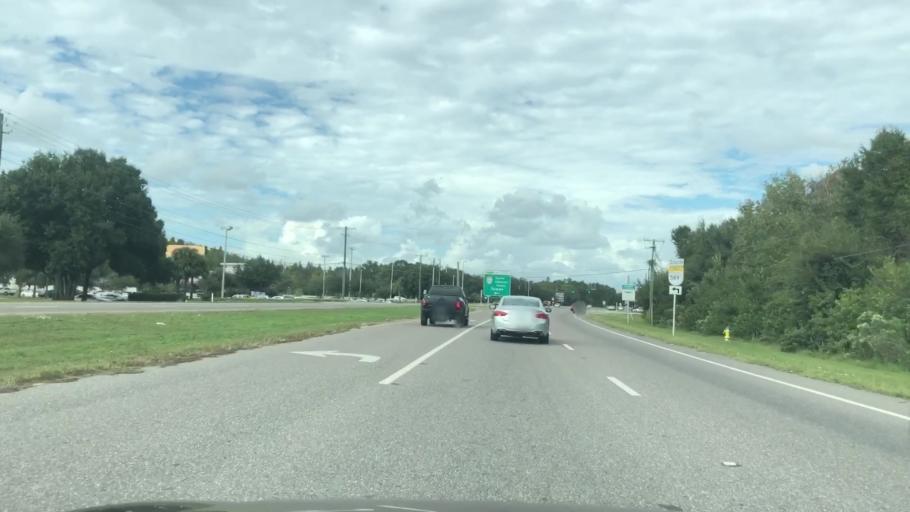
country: US
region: Florida
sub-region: Hillsborough County
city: Egypt Lake-Leto
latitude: 28.0332
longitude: -82.5409
